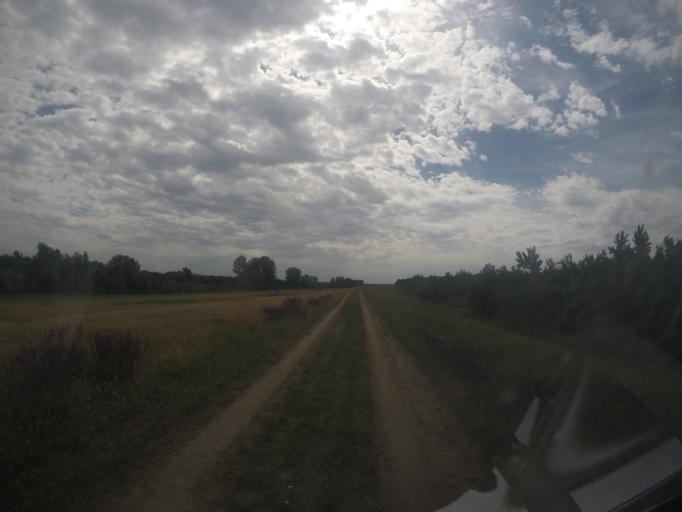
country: RS
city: Surduk
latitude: 45.1019
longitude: 20.3167
